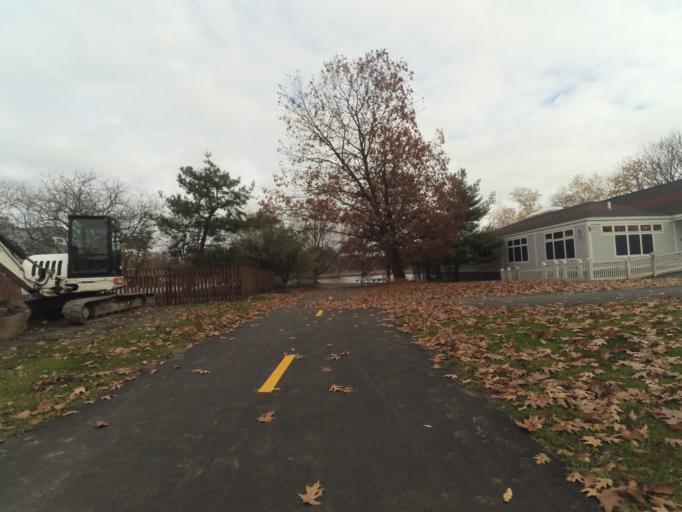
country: US
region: Massachusetts
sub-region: Middlesex County
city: Cambridge
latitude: 42.3706
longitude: -71.1333
